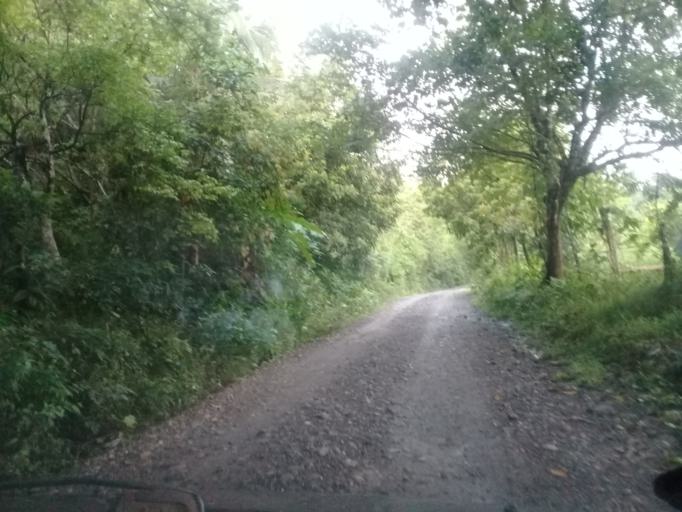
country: CO
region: Antioquia
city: Puerto Triunfo
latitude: 5.7325
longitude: -74.4739
